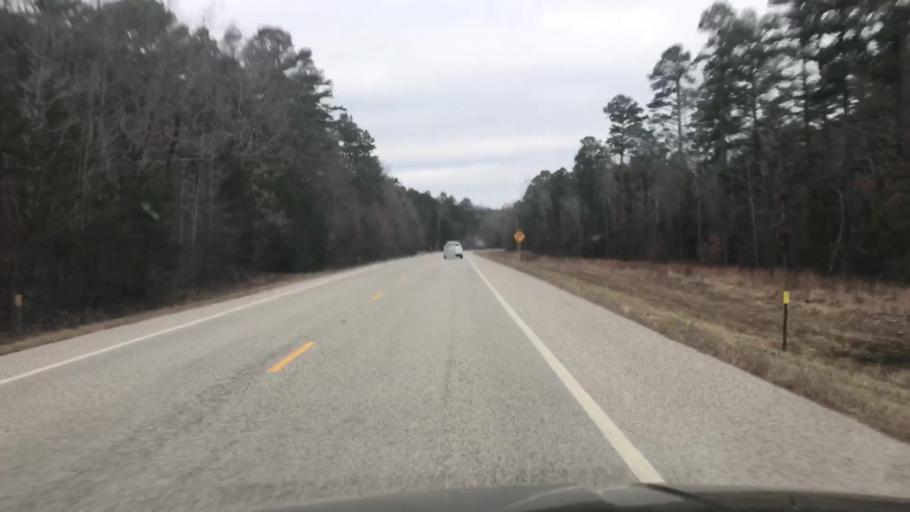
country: US
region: Arkansas
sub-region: Scott County
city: Waldron
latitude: 34.7143
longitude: -93.9445
